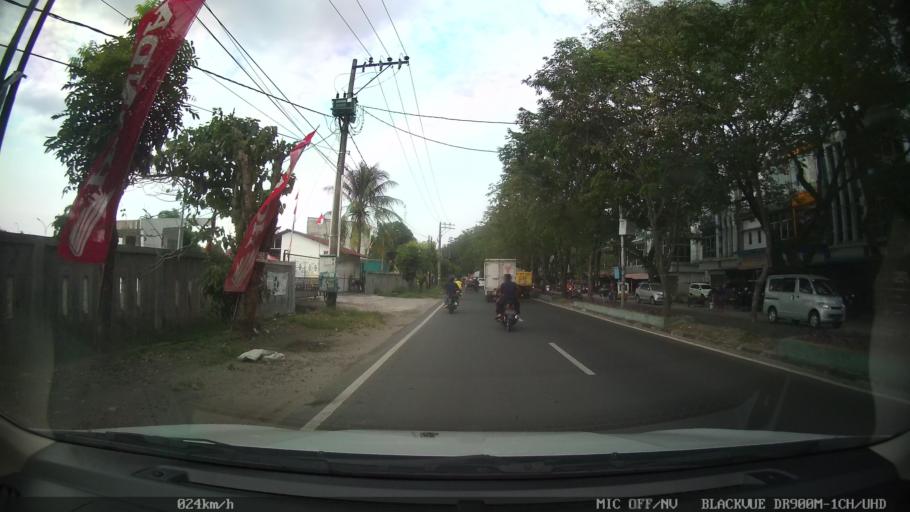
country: ID
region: North Sumatra
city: Sunggal
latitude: 3.5442
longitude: 98.6048
